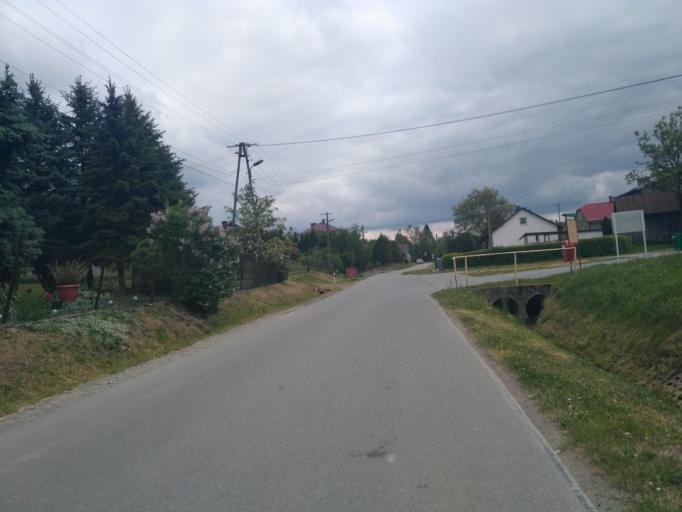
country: PL
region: Subcarpathian Voivodeship
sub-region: Powiat krosnienski
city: Jedlicze
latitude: 49.6889
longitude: 21.6400
